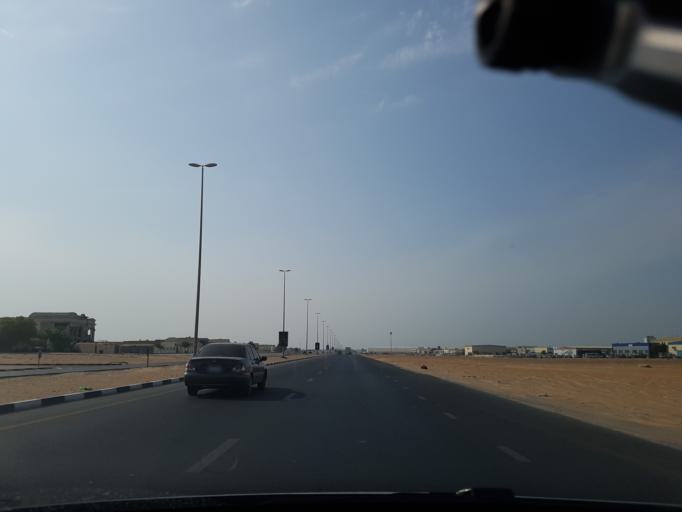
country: AE
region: Ajman
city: Ajman
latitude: 25.4285
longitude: 55.5179
